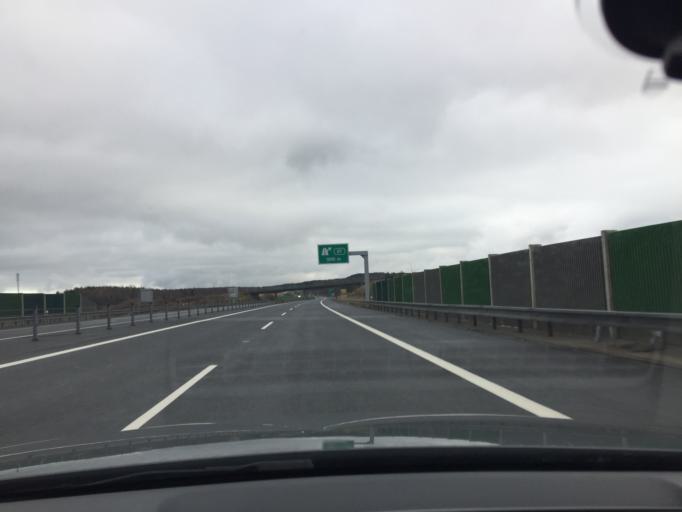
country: CZ
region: Ustecky
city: Chlumec
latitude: 50.7740
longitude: 13.9478
